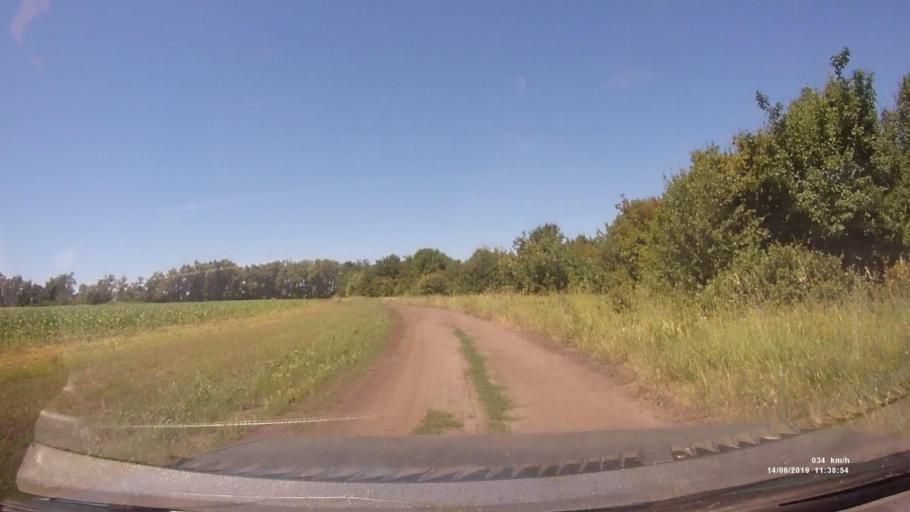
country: RU
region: Rostov
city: Kazanskaya
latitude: 49.8685
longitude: 41.3690
